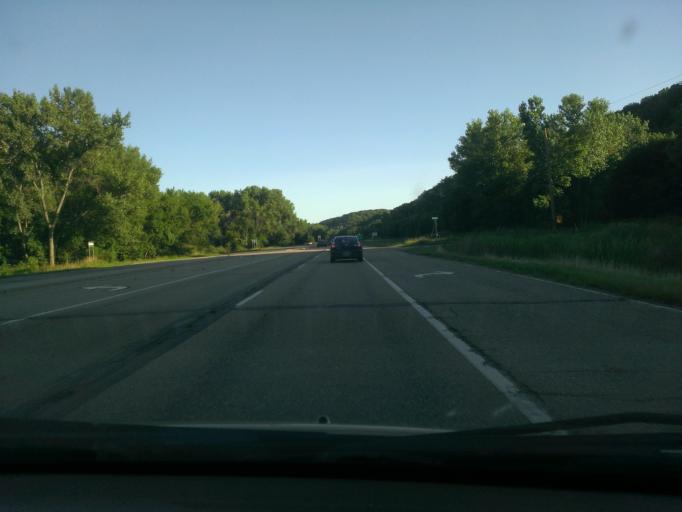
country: US
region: Minnesota
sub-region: Nicollet County
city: North Mankato
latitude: 44.2256
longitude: -94.0275
